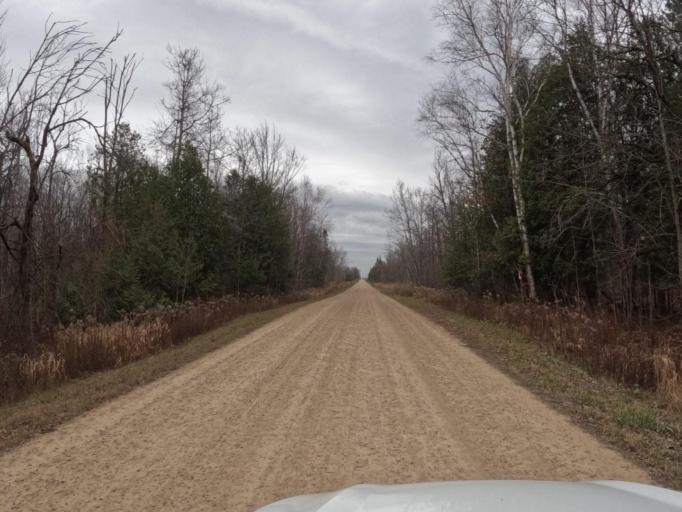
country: CA
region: Ontario
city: Shelburne
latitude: 44.0299
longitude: -80.3940
